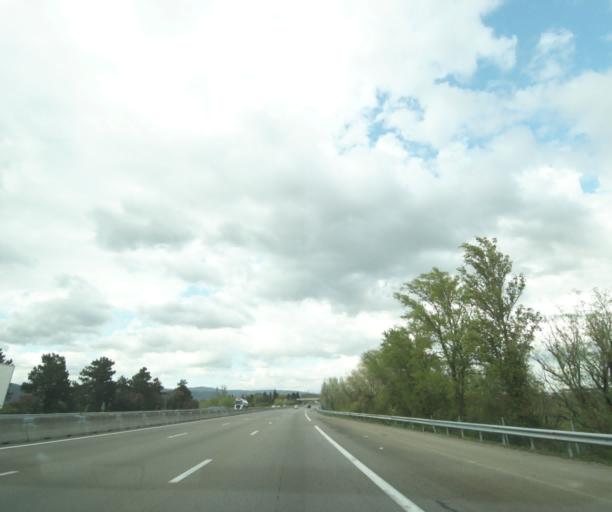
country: FR
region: Rhone-Alpes
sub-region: Departement de la Drome
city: Loriol-sur-Drome
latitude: 44.7453
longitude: 4.7892
